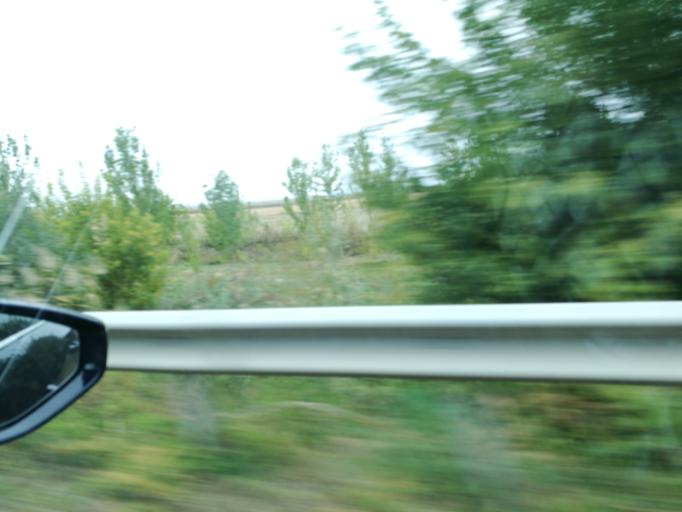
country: RO
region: Tulcea
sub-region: Oras Macin
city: Macin
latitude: 45.2603
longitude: 28.0678
